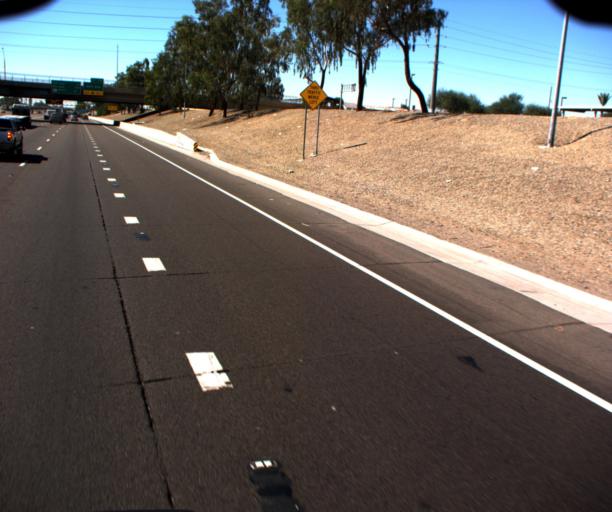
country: US
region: Arizona
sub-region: Maricopa County
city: Tolleson
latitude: 33.4628
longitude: -112.2279
